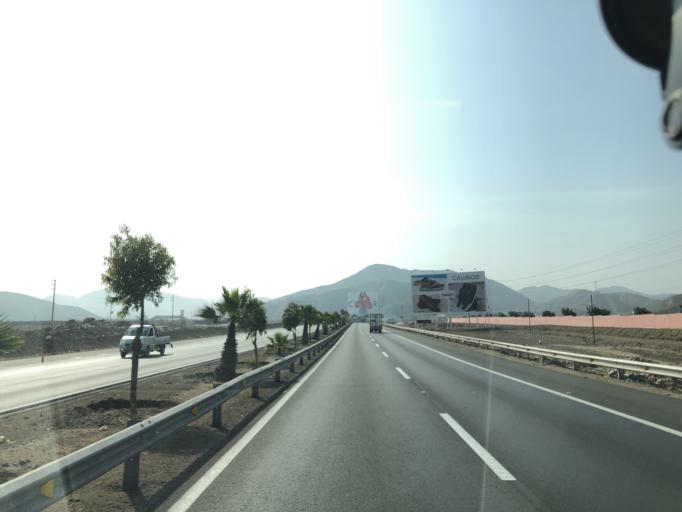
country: PE
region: Lima
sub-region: Lima
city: San Bartolo
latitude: -12.3948
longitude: -76.7604
